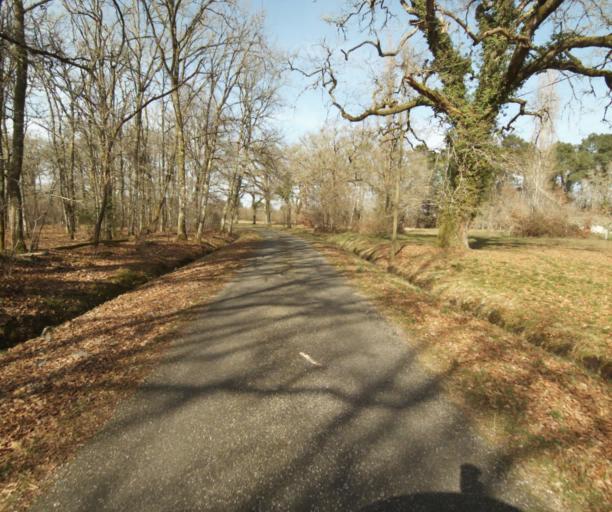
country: FR
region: Aquitaine
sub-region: Departement des Landes
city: Roquefort
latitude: 44.1500
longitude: -0.2064
